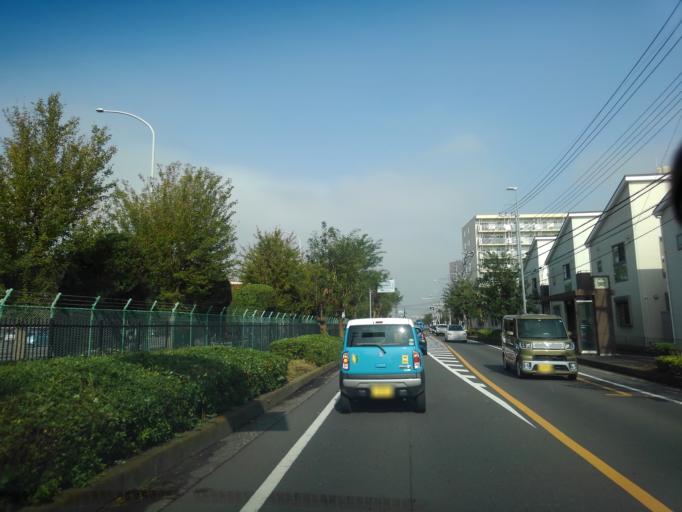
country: JP
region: Saitama
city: Tokorozawa
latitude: 35.8010
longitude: 139.4799
